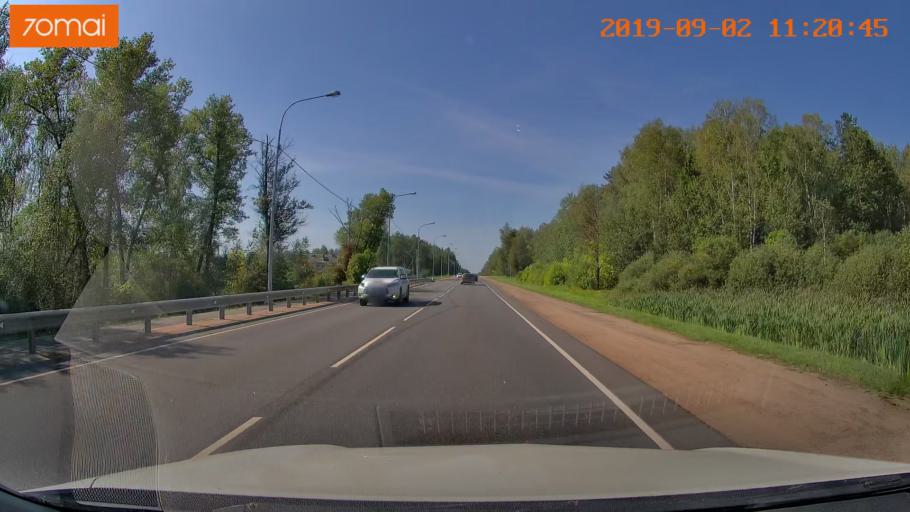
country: RU
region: Smolensk
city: Roslavl'
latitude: 54.0401
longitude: 33.0487
